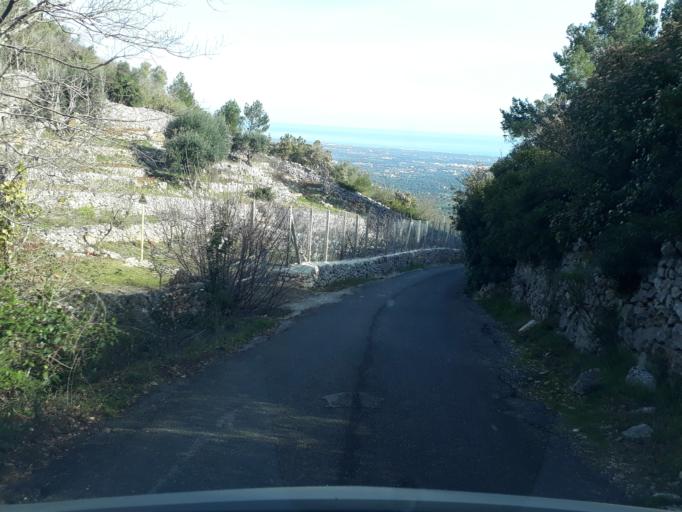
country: IT
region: Apulia
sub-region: Provincia di Brindisi
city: Lamie di Olimpie-Selva
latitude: 40.7885
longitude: 17.3677
